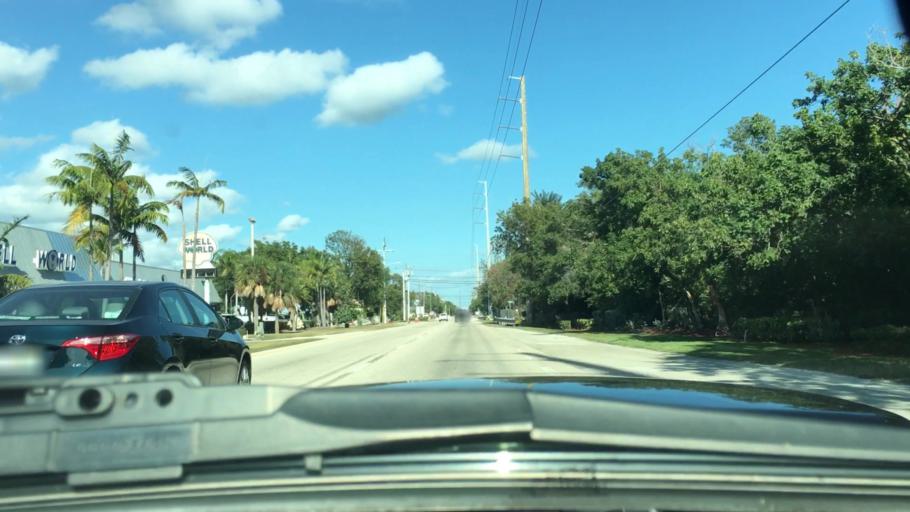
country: US
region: Florida
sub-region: Monroe County
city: Key Largo
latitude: 25.0737
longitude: -80.4629
